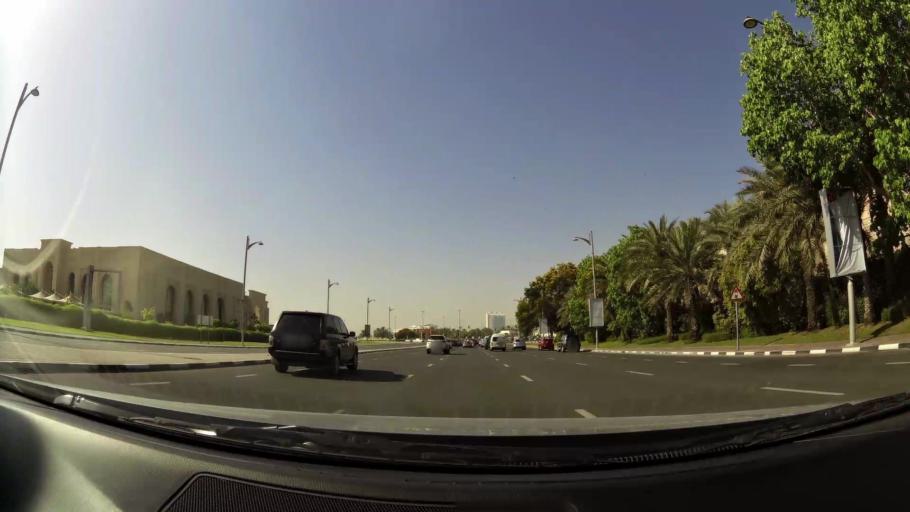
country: AE
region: Dubai
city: Dubai
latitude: 25.1347
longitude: 55.1880
